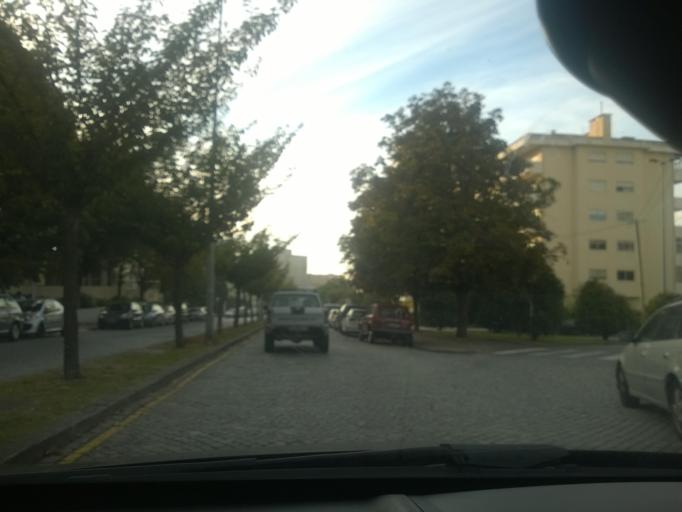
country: PT
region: Porto
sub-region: Matosinhos
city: Senhora da Hora
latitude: 41.1573
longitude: -8.6426
